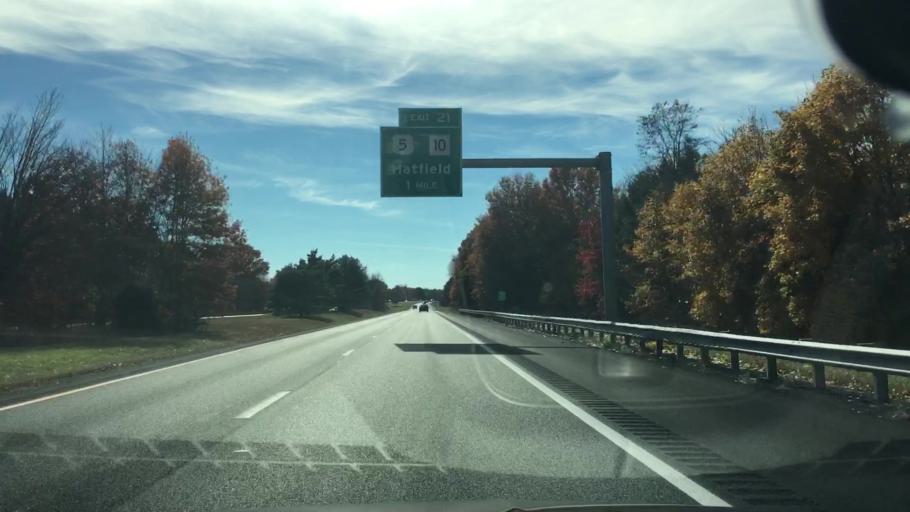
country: US
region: Massachusetts
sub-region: Hampshire County
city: Hatfield
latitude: 42.3770
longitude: -72.6326
